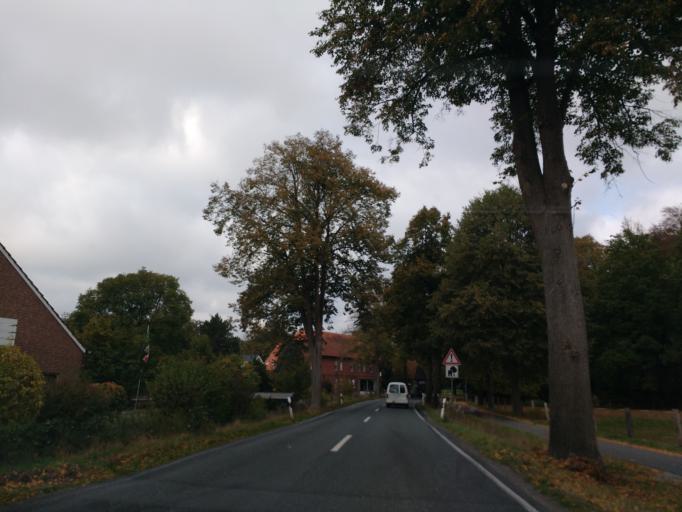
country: DE
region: North Rhine-Westphalia
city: Halle
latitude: 52.0401
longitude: 8.3308
